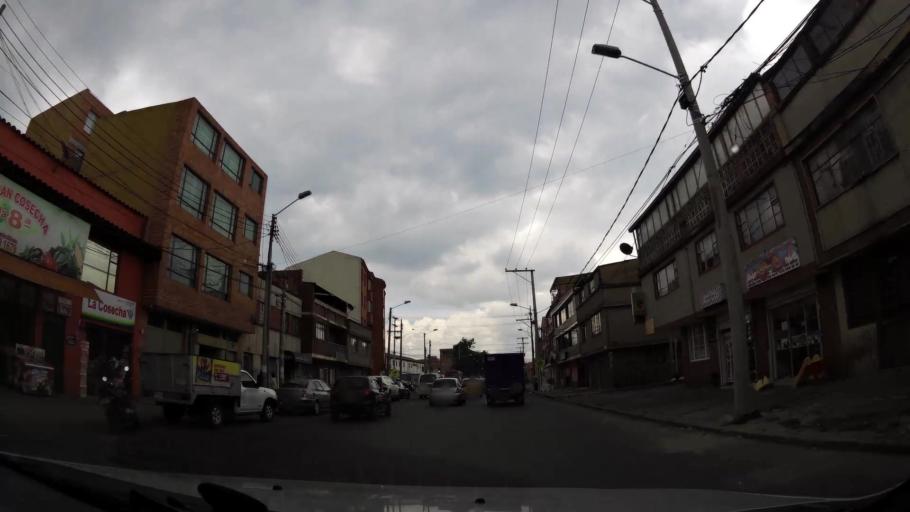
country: CO
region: Bogota D.C.
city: Bogota
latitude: 4.5813
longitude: -74.0877
